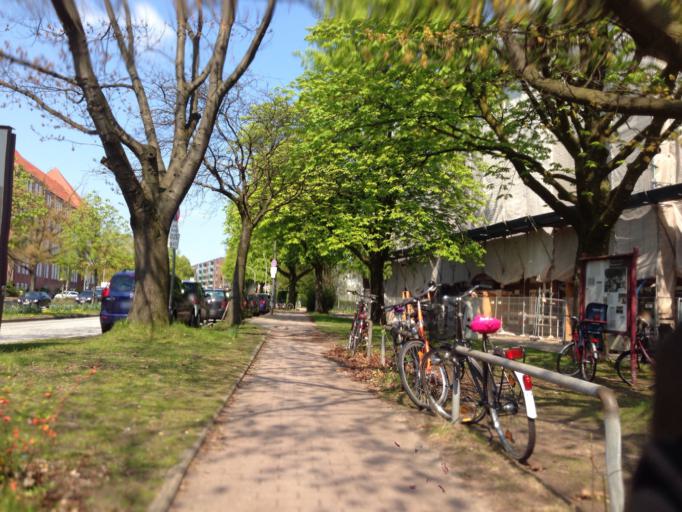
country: DE
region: Hamburg
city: Hamburg
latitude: 53.5827
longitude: 10.0336
